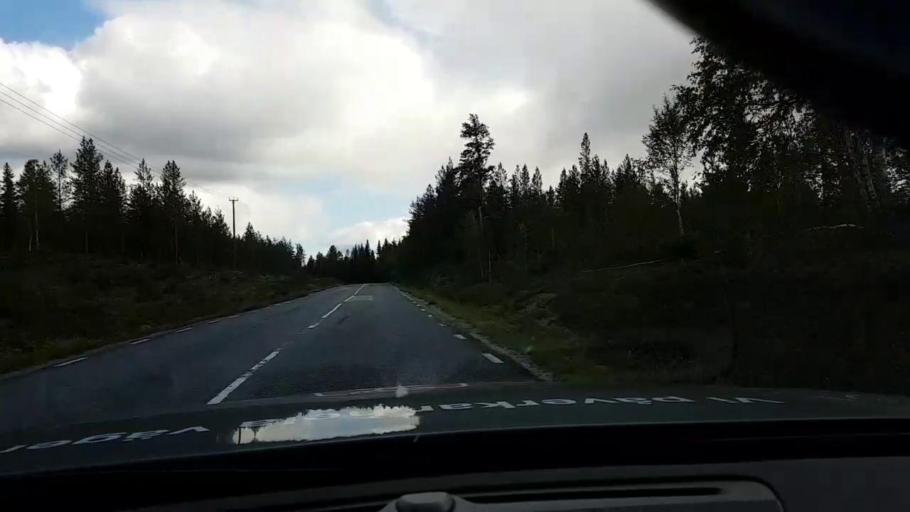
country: SE
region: Vaesterbotten
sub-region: Asele Kommun
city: Asele
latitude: 63.8001
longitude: 17.5564
